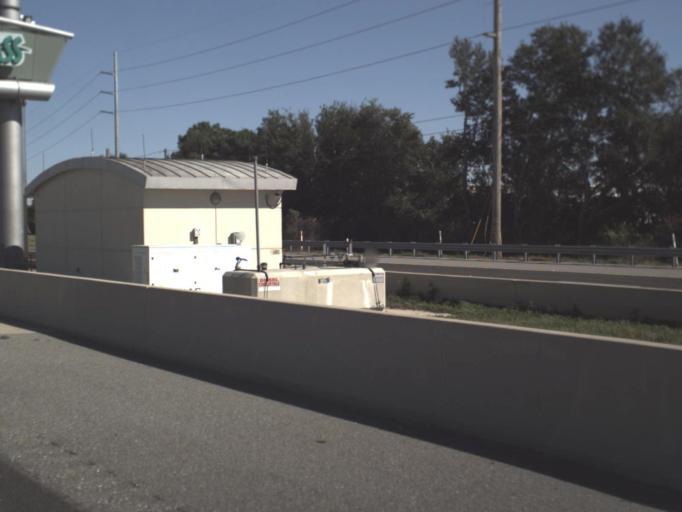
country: US
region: Florida
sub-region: Orange County
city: Sky Lake
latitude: 28.4438
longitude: -81.3851
